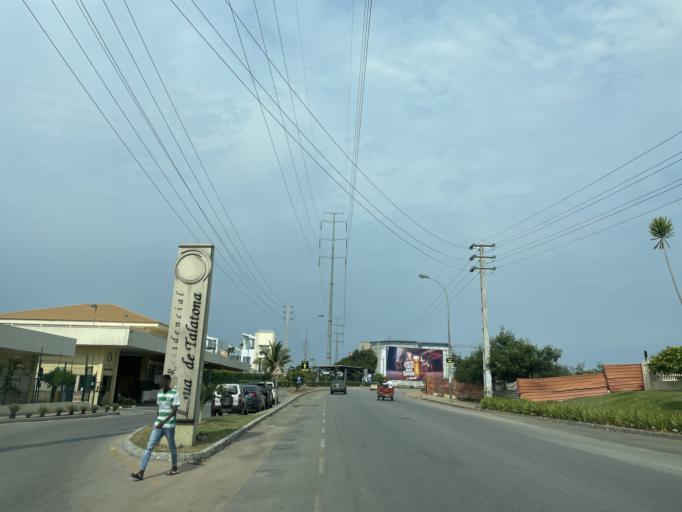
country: AO
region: Luanda
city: Luanda
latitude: -8.9212
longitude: 13.1884
